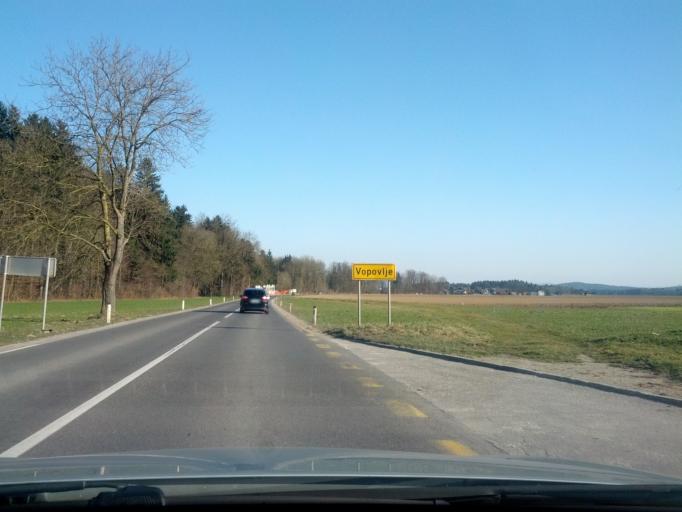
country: SI
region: Cerklje na Gorenjskem
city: Cerklje na Gorenjskem
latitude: 46.2248
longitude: 14.4919
